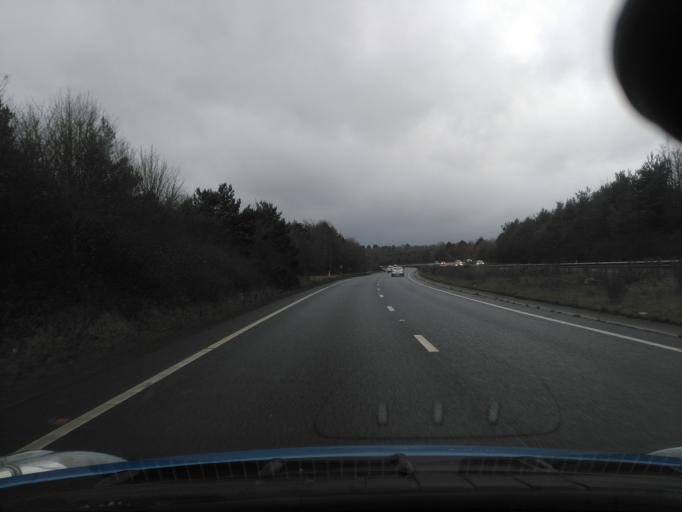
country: GB
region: England
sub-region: Surrey
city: Milford
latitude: 51.1785
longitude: -0.6529
